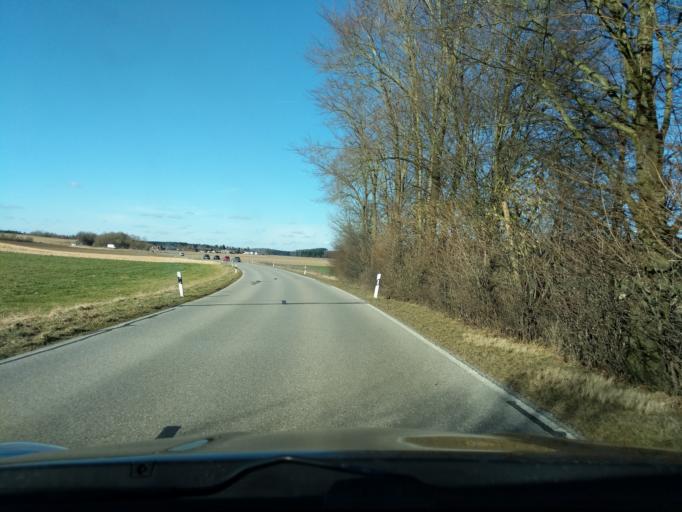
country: DE
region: Bavaria
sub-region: Upper Bavaria
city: Zorneding
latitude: 48.0978
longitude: 11.8335
